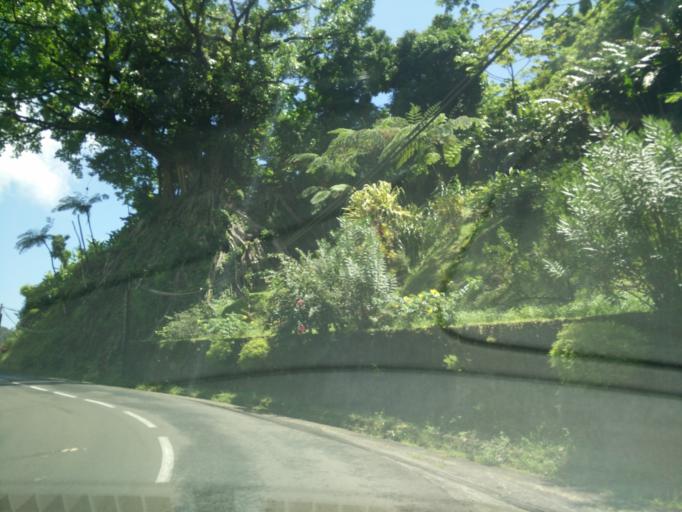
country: MQ
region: Martinique
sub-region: Martinique
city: Le Morne-Rouge
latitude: 14.7393
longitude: -61.1333
